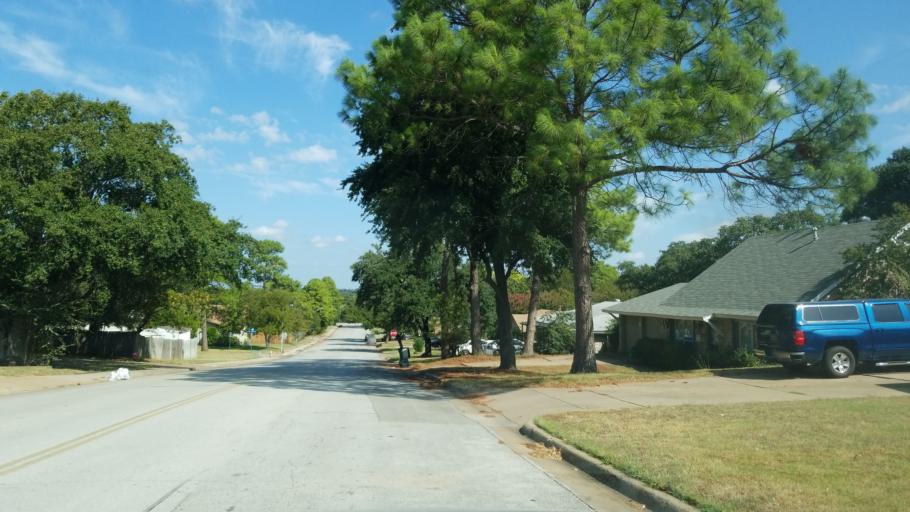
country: US
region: Texas
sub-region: Tarrant County
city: Euless
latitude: 32.8562
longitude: -97.0903
